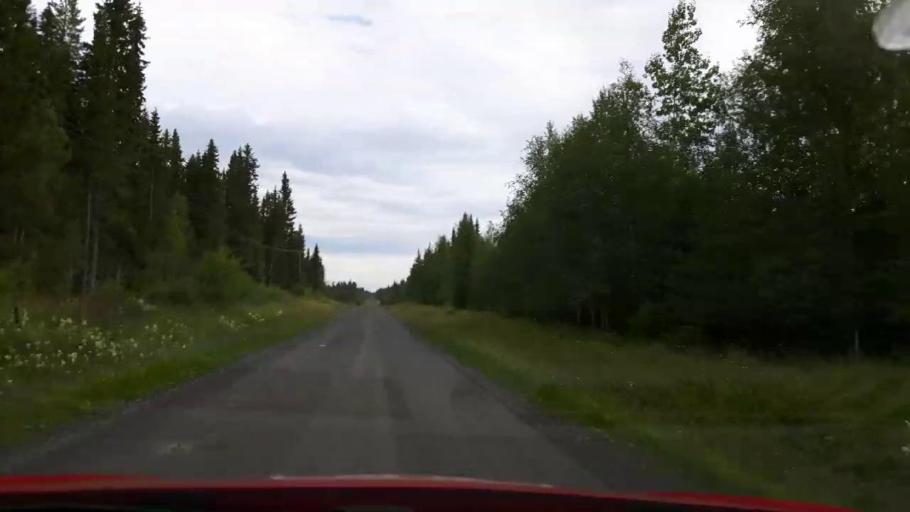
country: SE
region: Jaemtland
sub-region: Stroemsunds Kommun
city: Stroemsund
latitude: 63.5014
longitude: 15.3307
